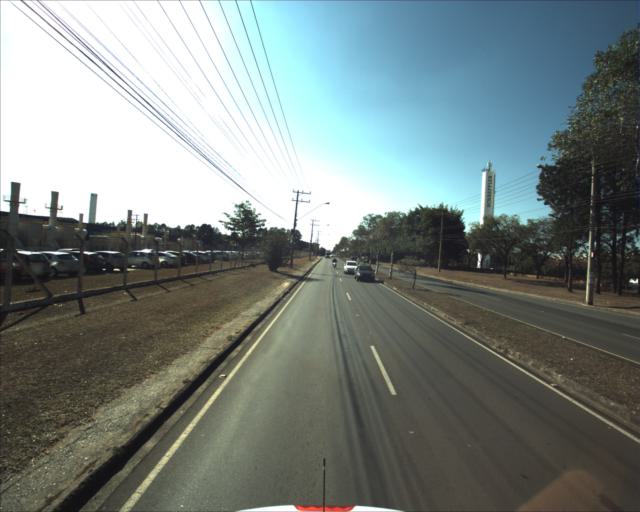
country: BR
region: Sao Paulo
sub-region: Sorocaba
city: Sorocaba
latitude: -23.4381
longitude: -47.4163
